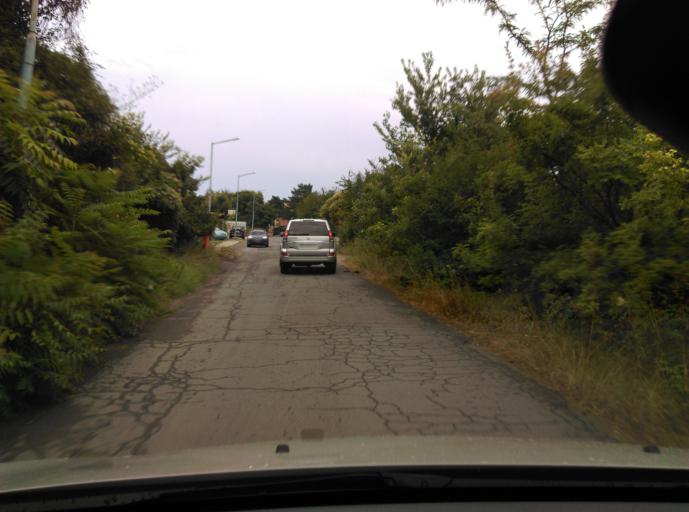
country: BG
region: Burgas
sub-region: Obshtina Sozopol
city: Sozopol
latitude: 42.4060
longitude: 27.7129
